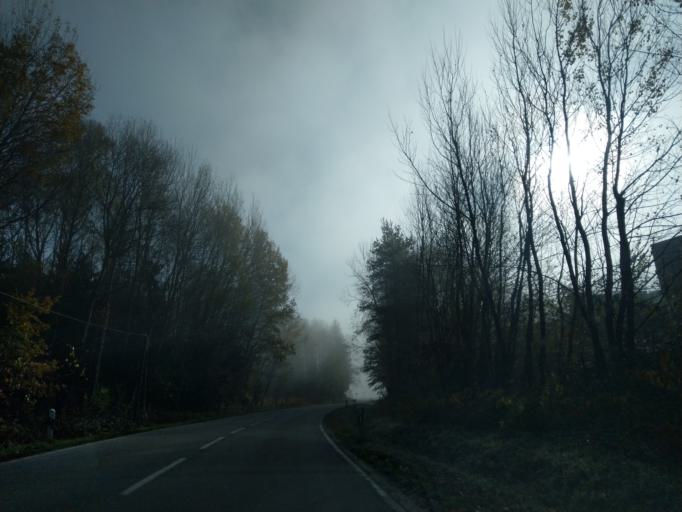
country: DE
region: Bavaria
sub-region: Lower Bavaria
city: Aussernzell
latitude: 48.7230
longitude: 13.2293
